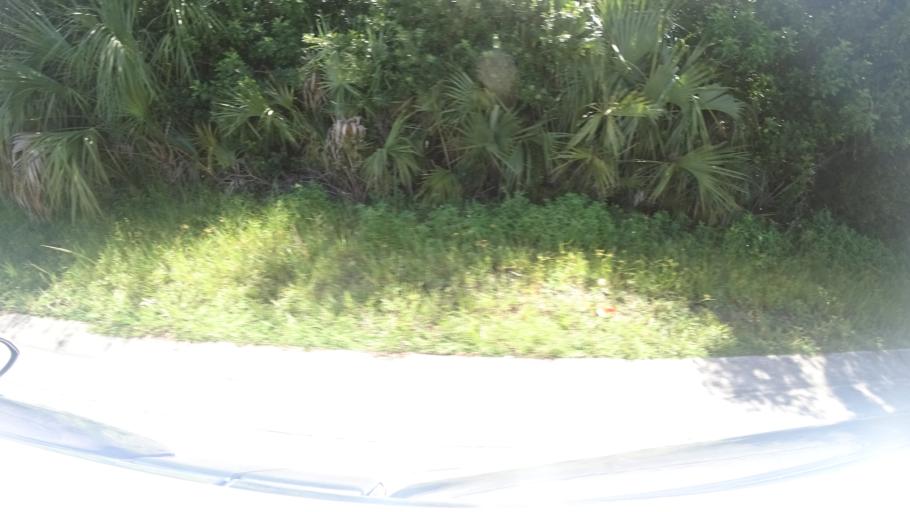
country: US
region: Florida
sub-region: Sarasota County
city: North Sarasota
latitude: 27.4050
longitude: -82.5308
